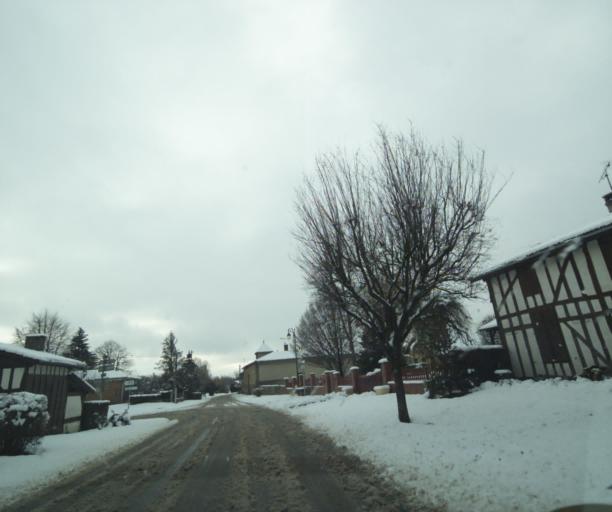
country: FR
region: Champagne-Ardenne
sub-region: Departement de la Haute-Marne
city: Montier-en-Der
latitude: 48.4950
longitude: 4.7010
